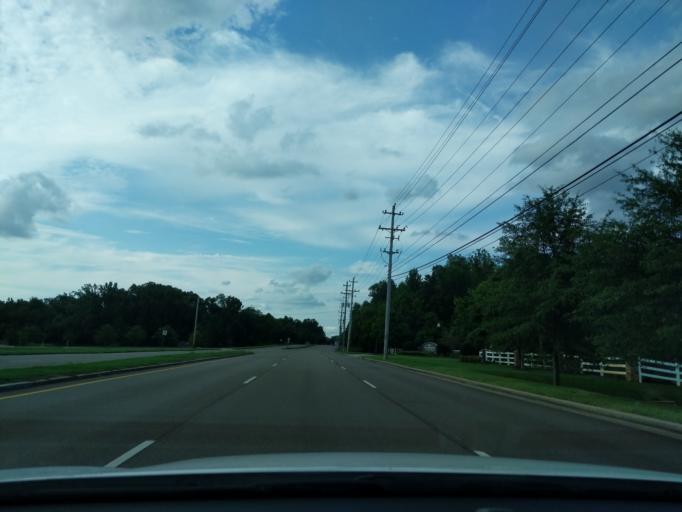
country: US
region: Tennessee
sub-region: Shelby County
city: Germantown
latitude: 35.0301
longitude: -89.7597
